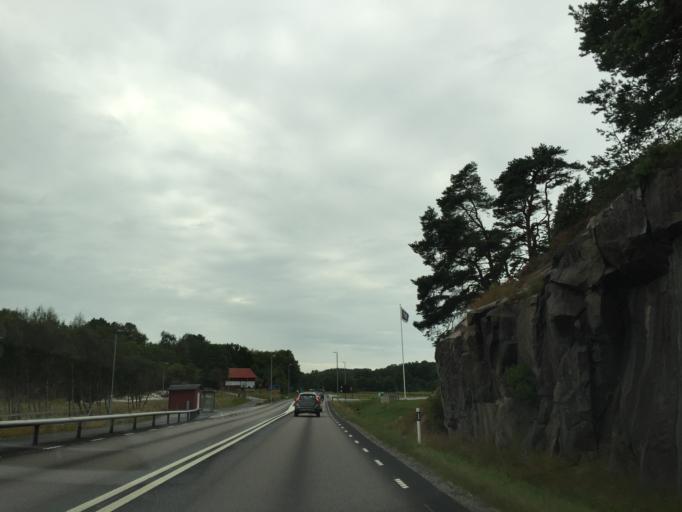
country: SE
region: Vaestra Goetaland
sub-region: Tjorns Kommun
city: Myggenas
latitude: 58.0490
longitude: 11.7537
